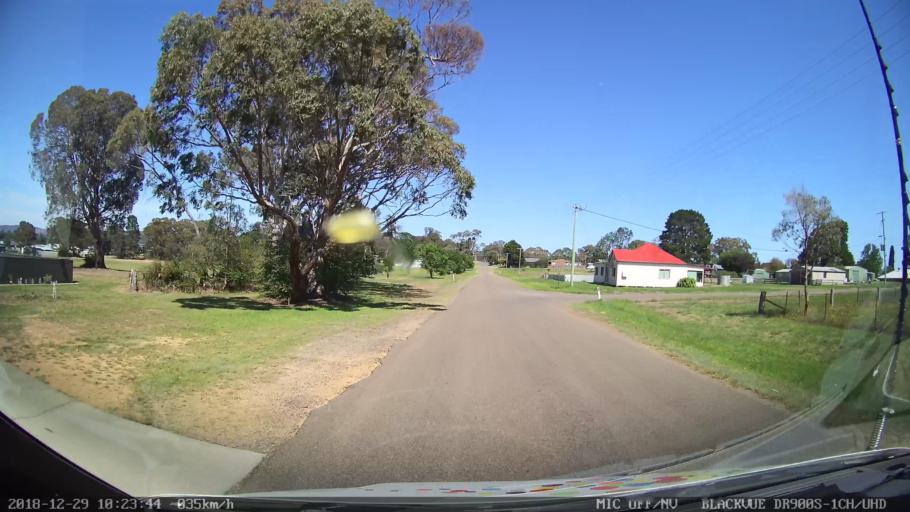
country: AU
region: New South Wales
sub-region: Yass Valley
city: Gundaroo
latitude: -34.9135
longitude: 149.4373
